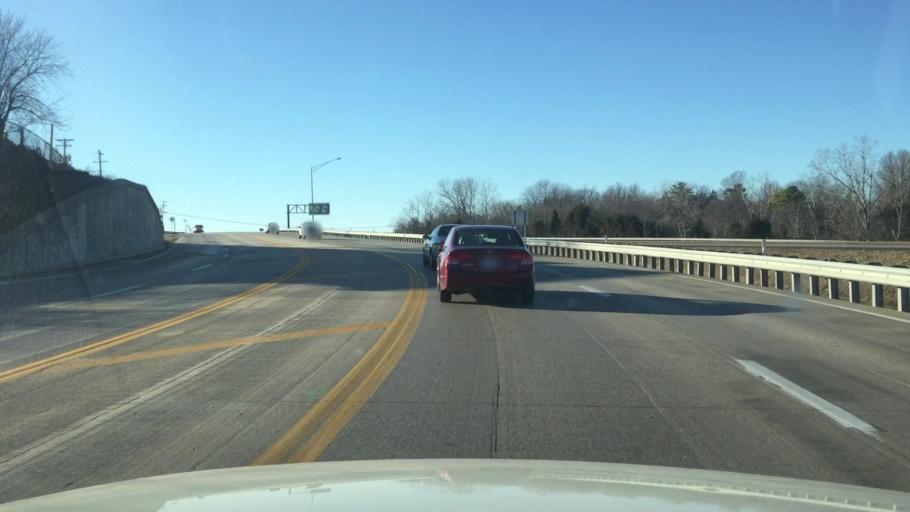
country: US
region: Missouri
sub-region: Cole County
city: Jefferson City
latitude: 38.5811
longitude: -92.2331
